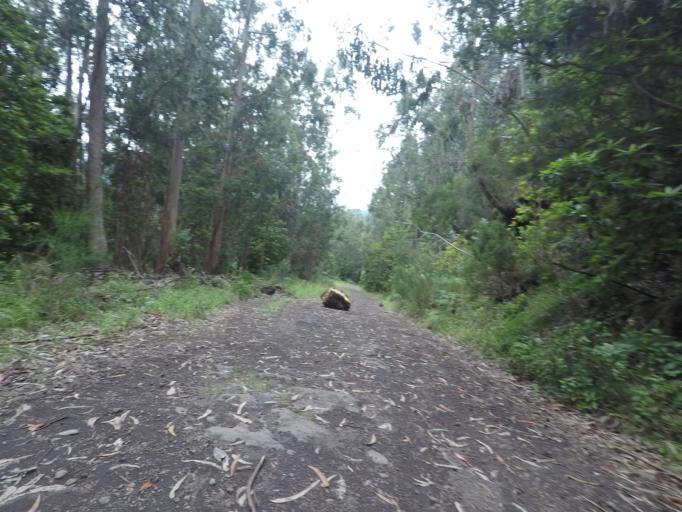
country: PT
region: Madeira
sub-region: Sao Vicente
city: Sao Vicente
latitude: 32.7771
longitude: -17.0508
